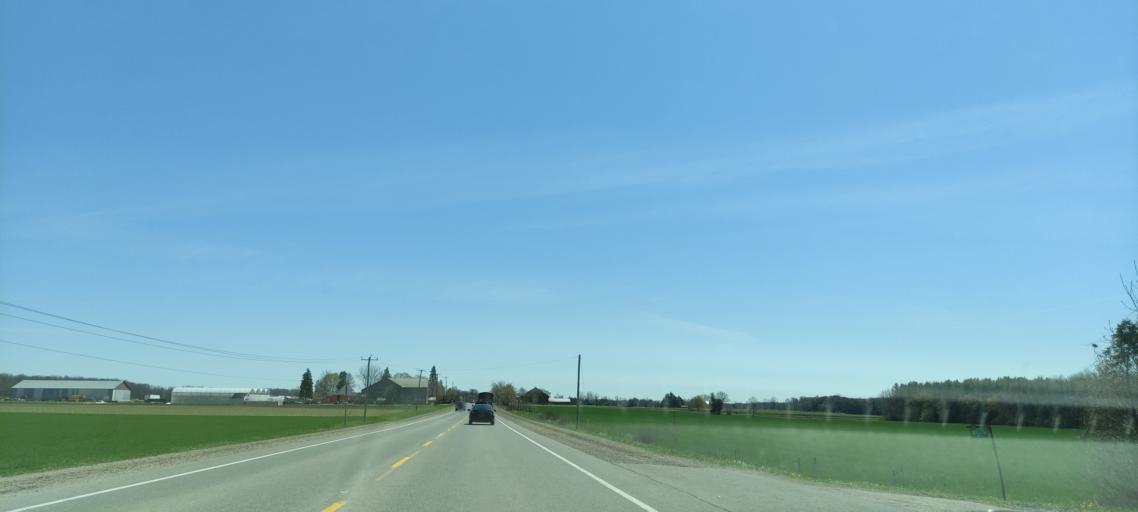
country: CA
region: Ontario
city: Waterloo
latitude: 43.5826
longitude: -80.4323
